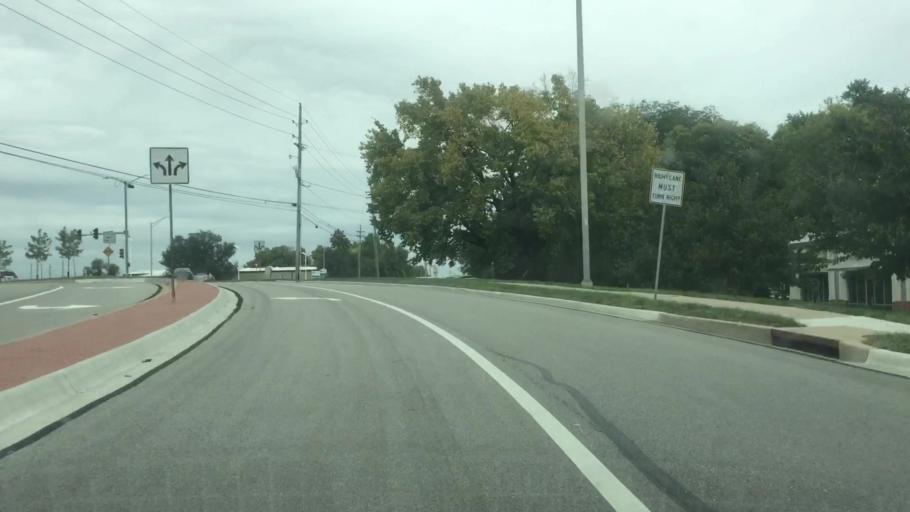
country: US
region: Kansas
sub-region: Johnson County
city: Lenexa
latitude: 38.9157
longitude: -94.7609
